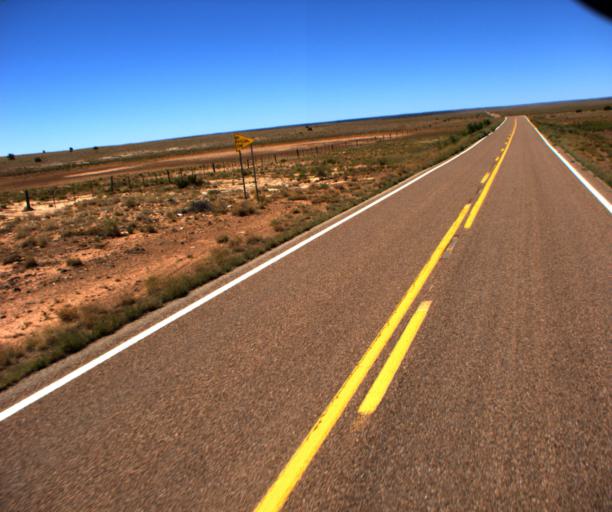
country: US
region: Arizona
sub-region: Navajo County
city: Winslow
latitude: 34.8594
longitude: -110.6623
